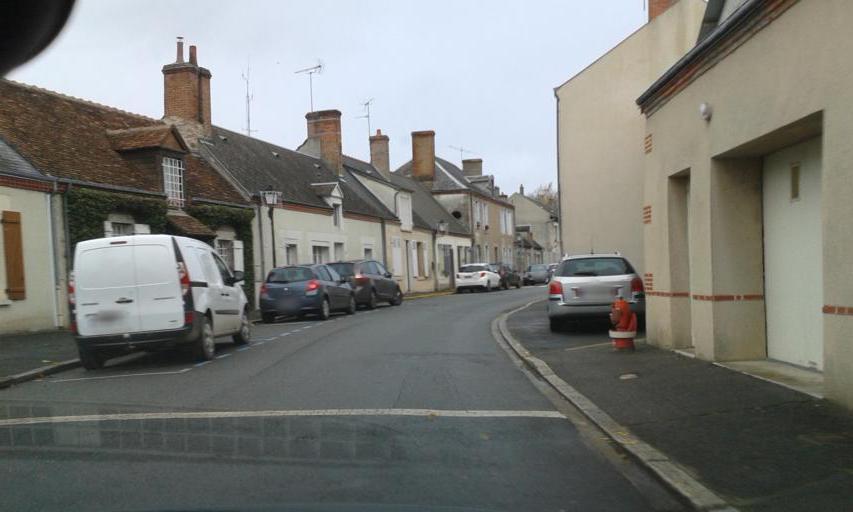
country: FR
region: Centre
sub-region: Departement du Loiret
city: Vitry-aux-Loges
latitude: 47.9394
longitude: 2.2663
